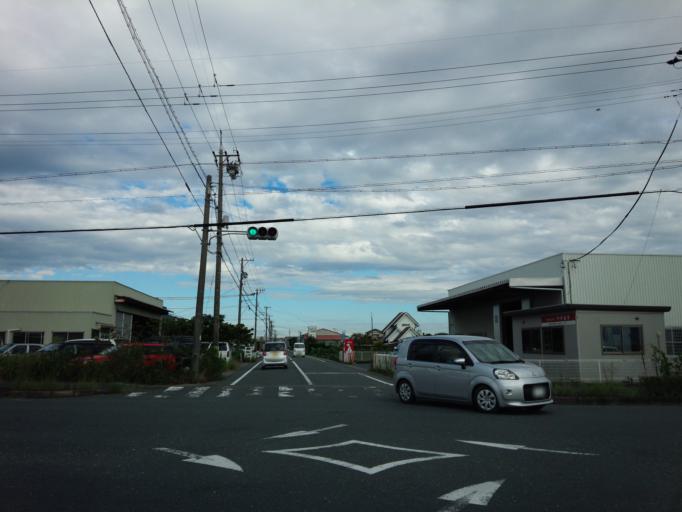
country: JP
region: Shizuoka
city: Hamakita
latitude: 34.7543
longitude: 137.7922
